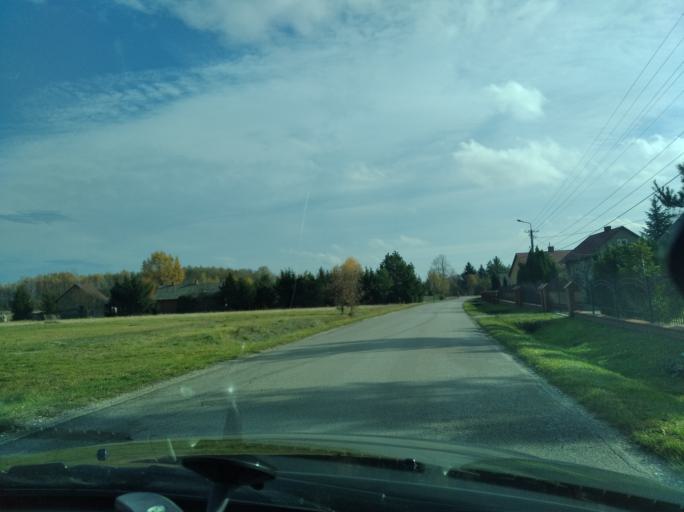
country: PL
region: Subcarpathian Voivodeship
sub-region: Powiat ropczycko-sedziszowski
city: Sedziszow Malopolski
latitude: 50.1193
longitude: 21.7267
